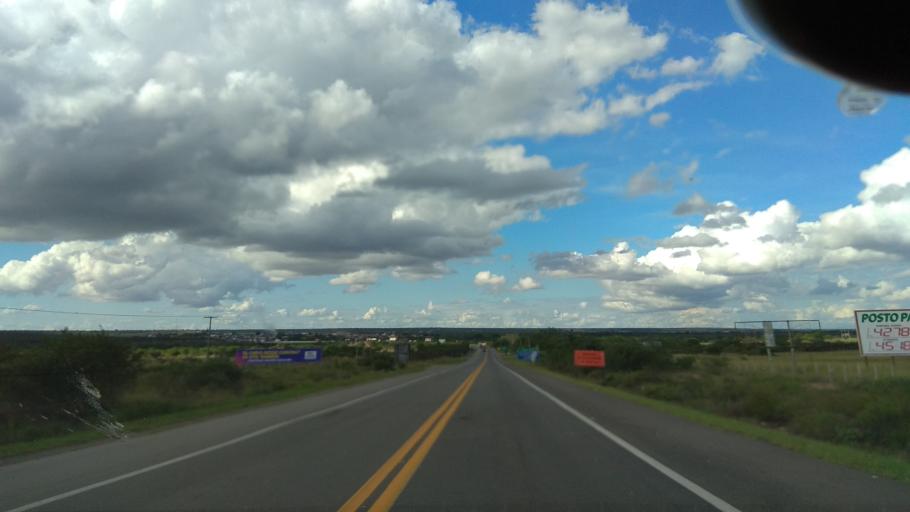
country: BR
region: Bahia
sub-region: Castro Alves
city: Castro Alves
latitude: -12.5939
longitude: -39.5309
